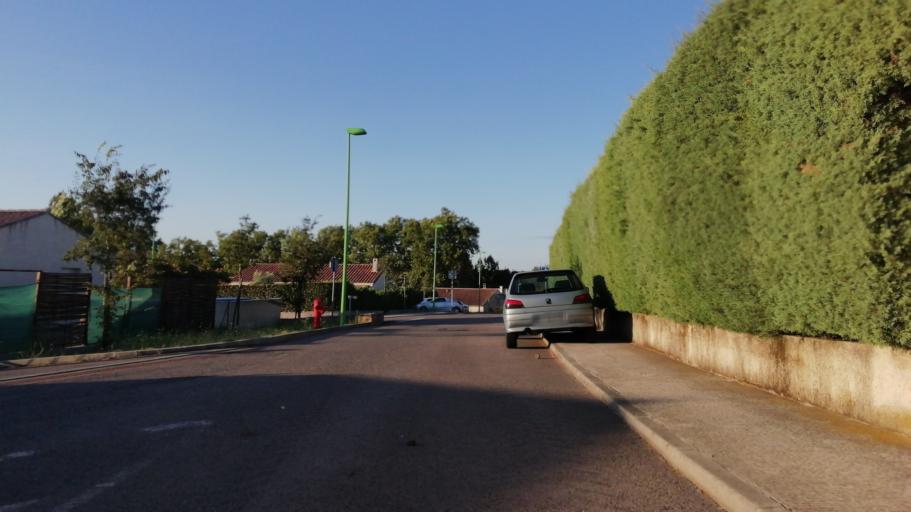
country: FR
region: Languedoc-Roussillon
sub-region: Departement de l'Herault
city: Saint-Martin-de-Londres
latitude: 43.7849
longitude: 3.7342
